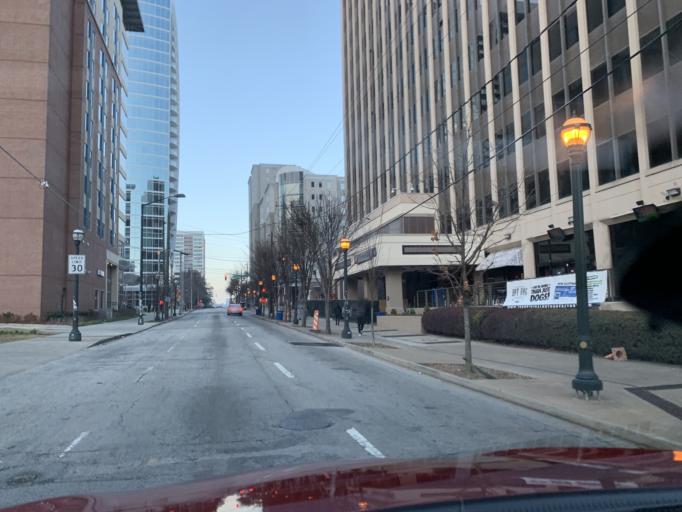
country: US
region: Georgia
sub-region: Fulton County
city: Atlanta
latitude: 33.7563
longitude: -84.3822
